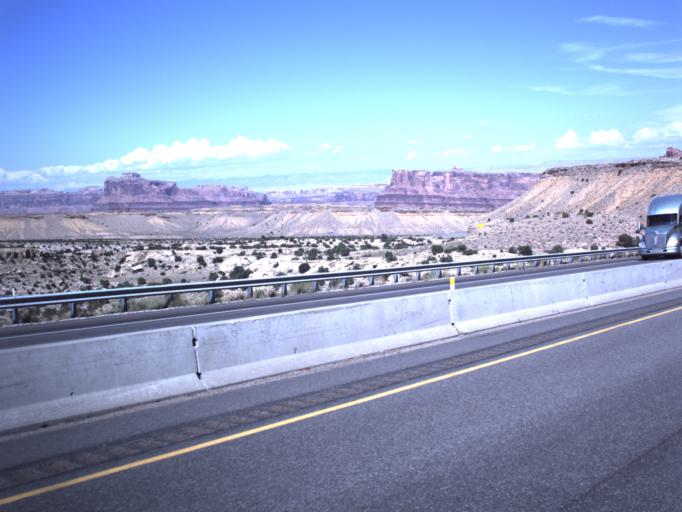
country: US
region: Utah
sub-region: Emery County
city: Castle Dale
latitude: 38.9299
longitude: -110.4920
